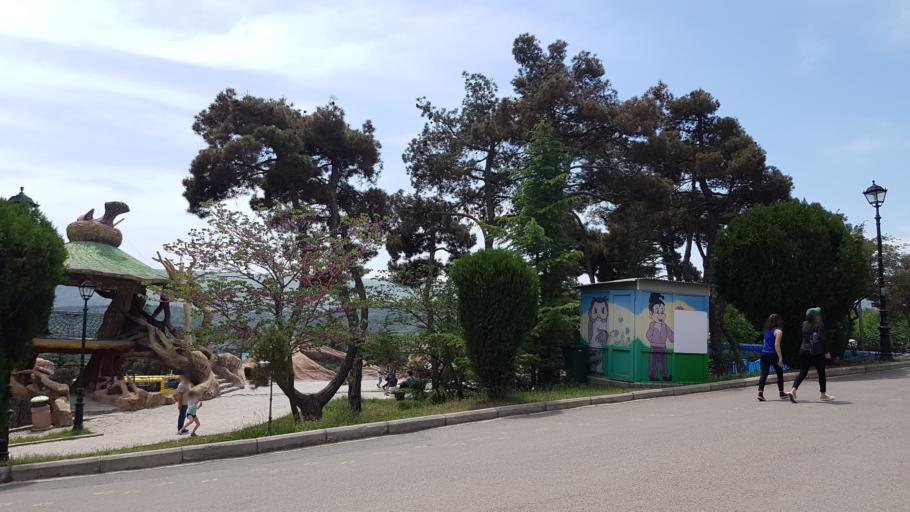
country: GE
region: T'bilisi
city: Tbilisi
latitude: 41.6942
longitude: 44.7825
